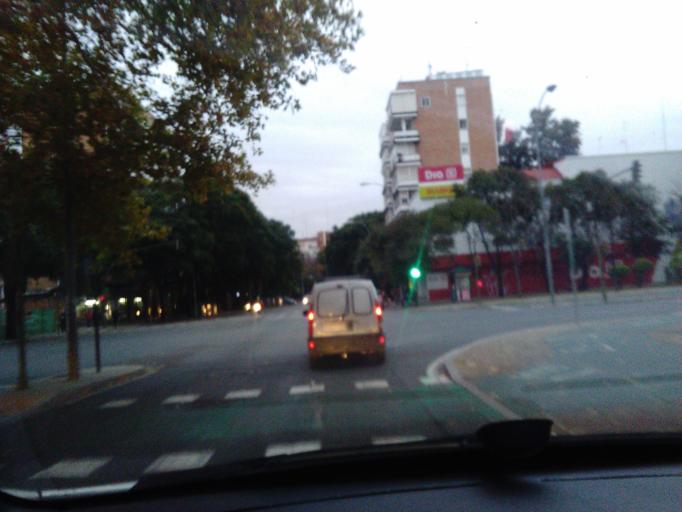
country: ES
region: Andalusia
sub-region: Provincia de Sevilla
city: Sevilla
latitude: 37.3752
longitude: -5.9673
